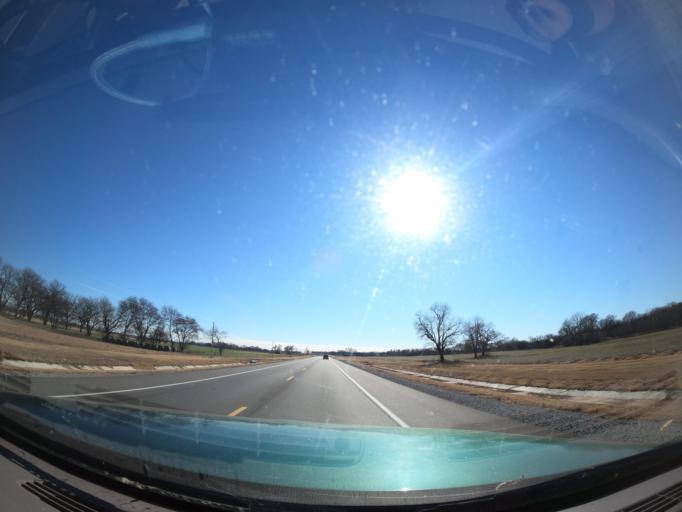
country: US
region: Oklahoma
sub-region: Wagoner County
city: Coweta
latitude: 35.8938
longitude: -95.6592
